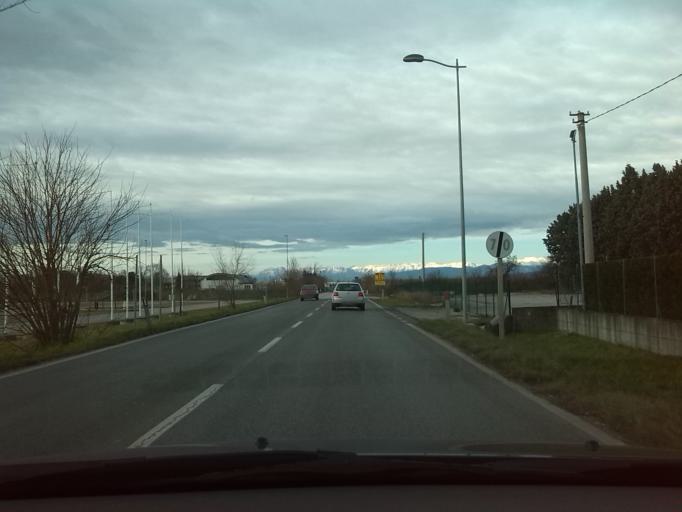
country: IT
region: Friuli Venezia Giulia
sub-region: Provincia di Gorizia
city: Sagrado
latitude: 45.8954
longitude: 13.4749
